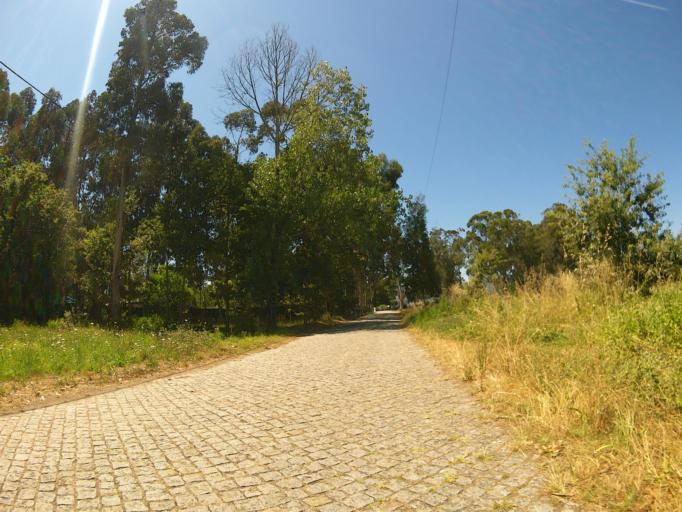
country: PT
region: Viana do Castelo
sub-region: Viana do Castelo
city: Darque
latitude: 41.6916
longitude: -8.7719
